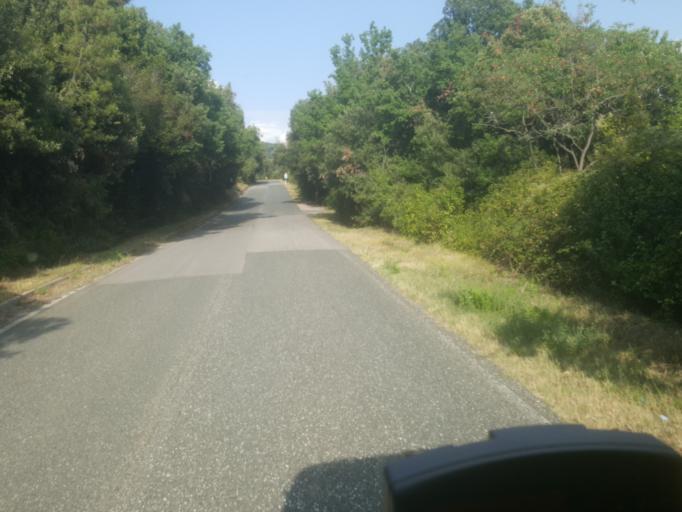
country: IT
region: Tuscany
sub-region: Province of Florence
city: Gambassi Terme
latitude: 43.4846
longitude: 10.9144
